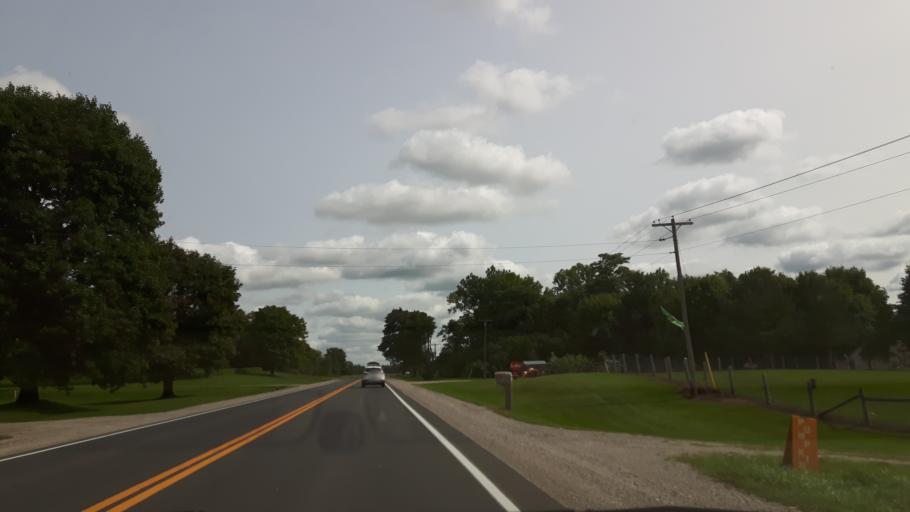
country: CA
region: Ontario
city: Bluewater
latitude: 43.5961
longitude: -81.4915
